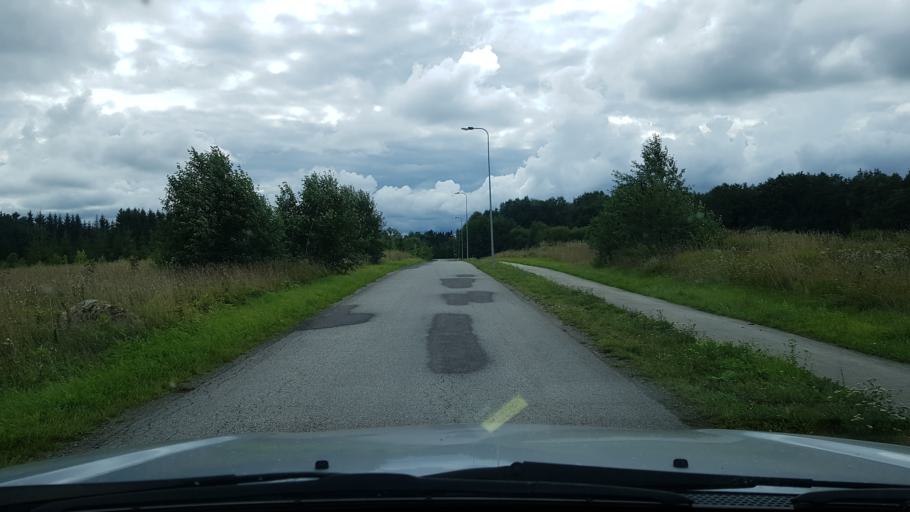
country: EE
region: Harju
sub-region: Rae vald
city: Vaida
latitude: 59.3160
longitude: 24.9478
